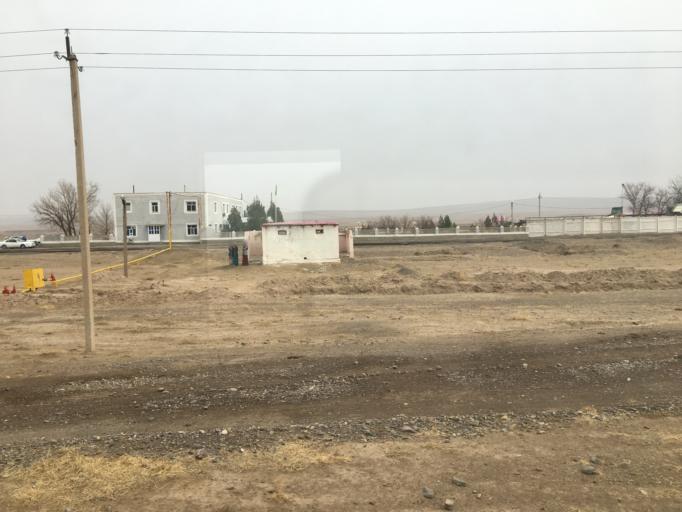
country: TM
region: Mary
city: Serhetabat
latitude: 35.6408
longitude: 62.5512
